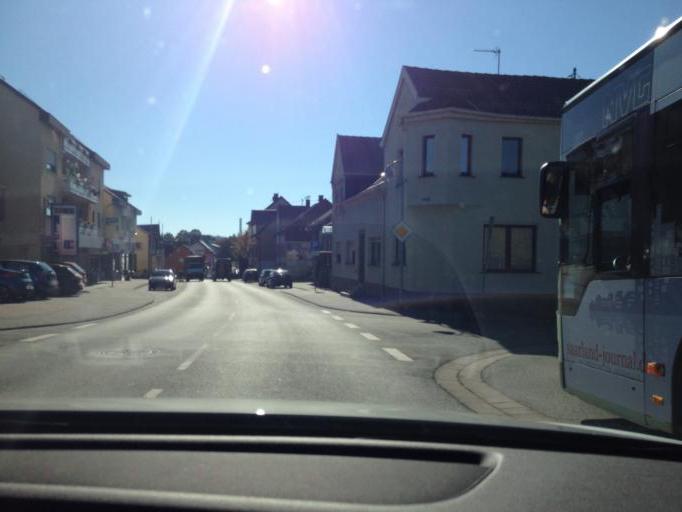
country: DE
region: Saarland
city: Merchweiler
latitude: 49.3573
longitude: 7.0563
